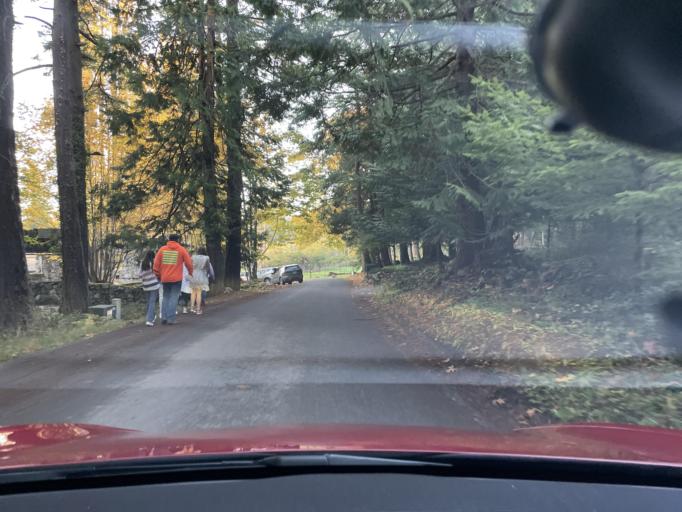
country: US
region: Washington
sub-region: San Juan County
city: Friday Harbor
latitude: 48.6163
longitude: -123.1518
